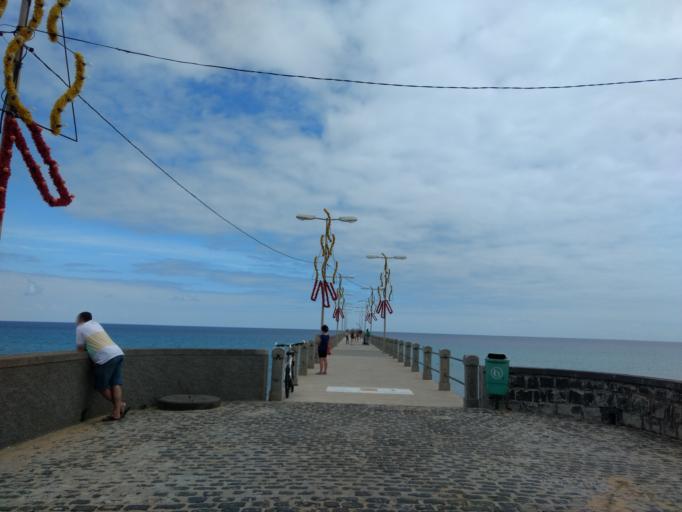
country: PT
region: Madeira
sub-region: Porto Santo
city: Vila de Porto Santo
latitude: 33.0577
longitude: -16.3347
